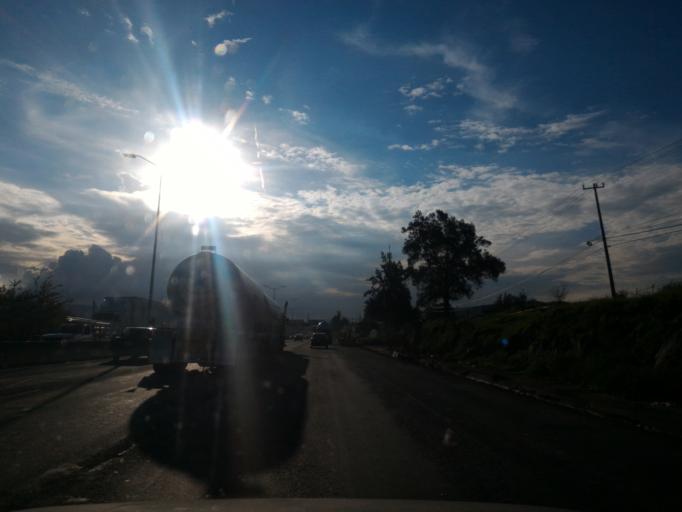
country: MX
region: Jalisco
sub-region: Tlajomulco de Zuniga
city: Altus Bosques
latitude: 20.5813
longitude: -103.3737
